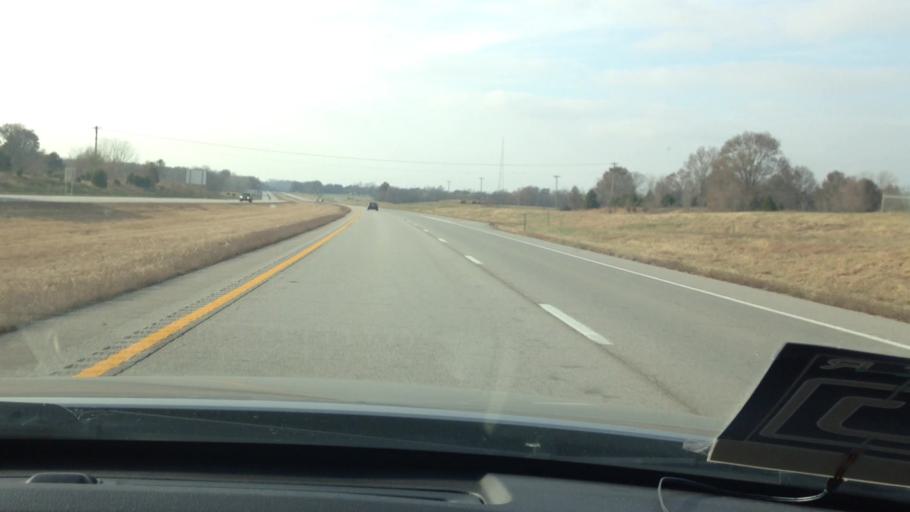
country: US
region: Missouri
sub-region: Cass County
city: Garden City
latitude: 38.5019
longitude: -94.0736
